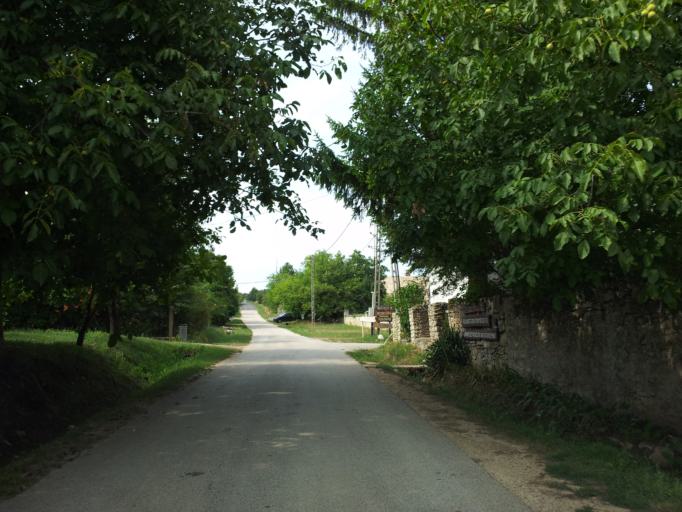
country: HU
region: Veszprem
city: Zanka
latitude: 46.9411
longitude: 17.7574
